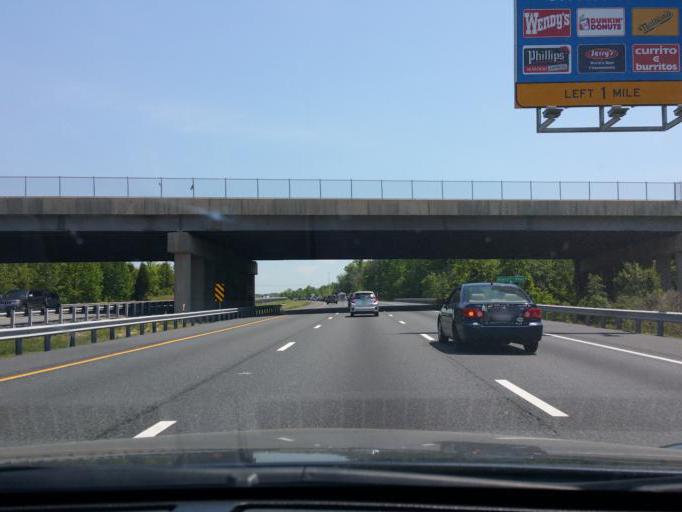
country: US
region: Maryland
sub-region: Harford County
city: Riverside
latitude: 39.4839
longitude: -76.2520
